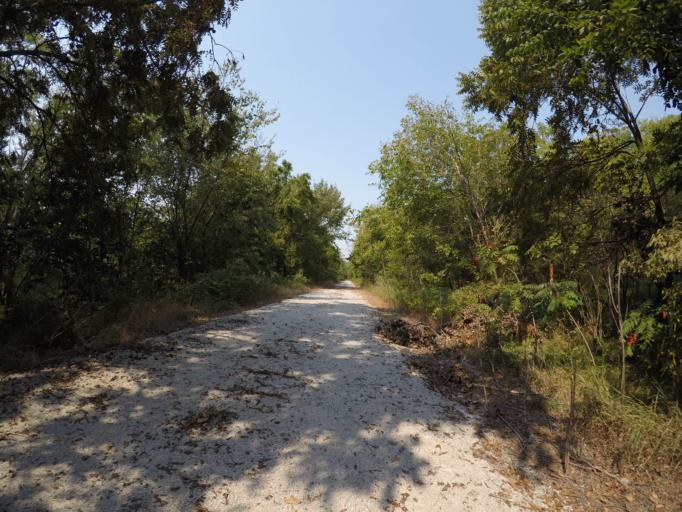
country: US
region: Nebraska
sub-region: Gage County
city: Beatrice
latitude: 40.2528
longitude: -96.7023
